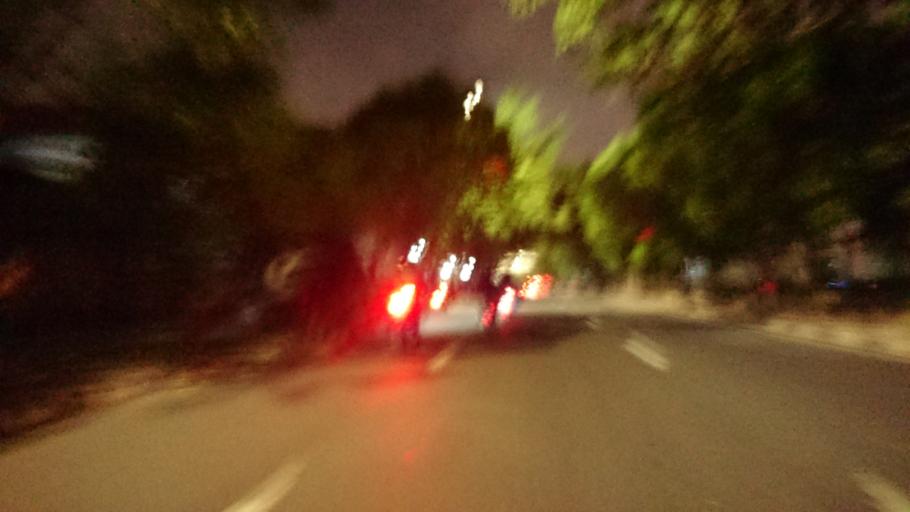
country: ID
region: Jakarta Raya
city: Jakarta
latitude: -6.2090
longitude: 106.7965
